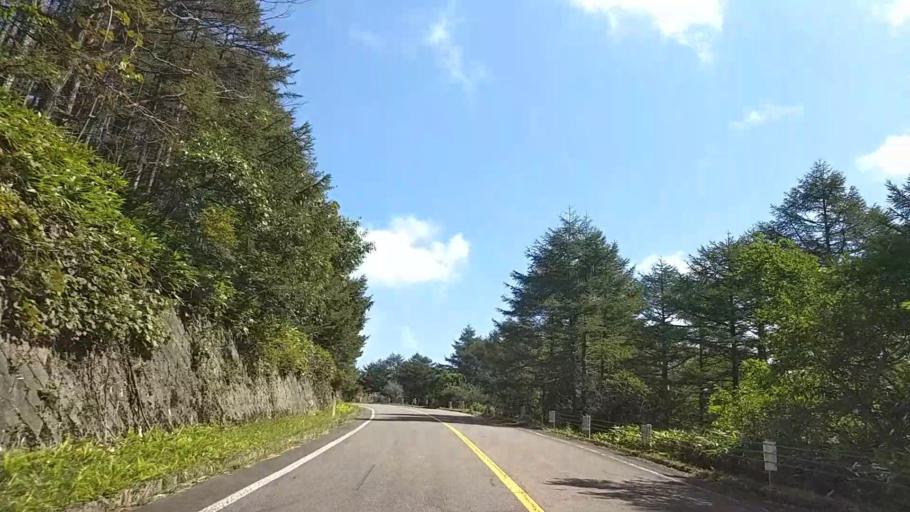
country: JP
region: Nagano
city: Suwa
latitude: 36.1500
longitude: 138.1406
